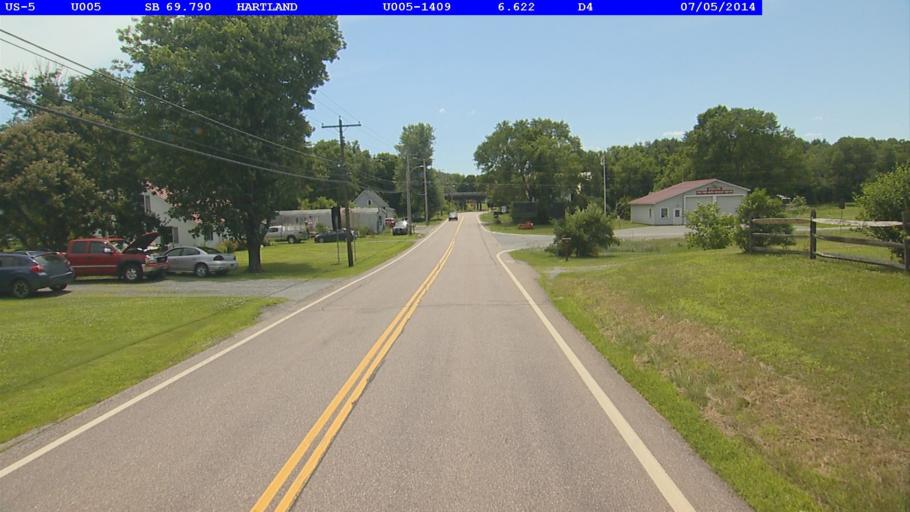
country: US
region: Vermont
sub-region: Windsor County
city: White River Junction
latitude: 43.5960
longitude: -72.3536
